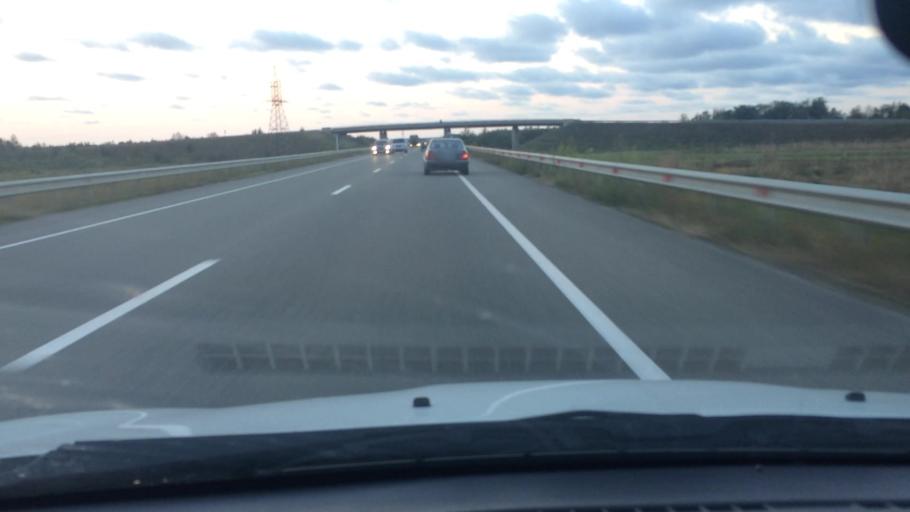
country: GE
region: Ajaria
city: Ochkhamuri
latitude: 41.8905
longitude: 41.8073
